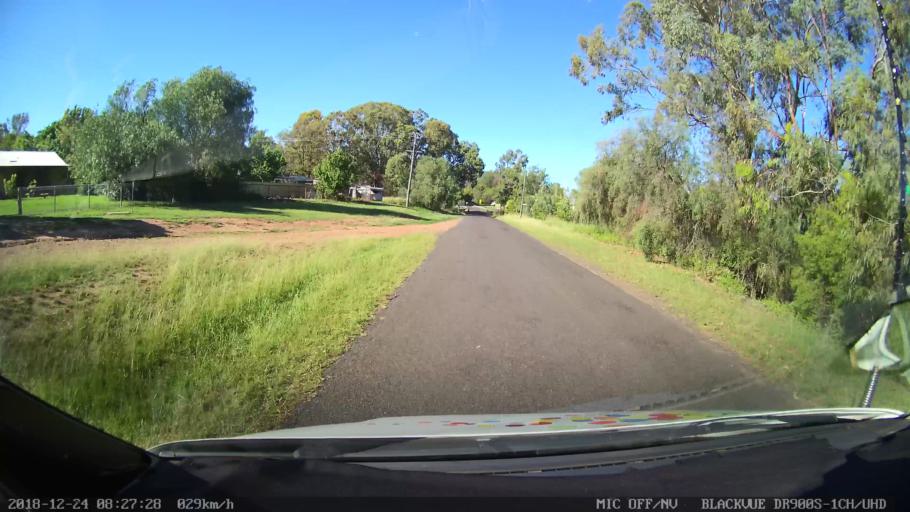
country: AU
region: New South Wales
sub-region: Tamworth Municipality
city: Phillip
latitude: -31.2610
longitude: 150.7368
